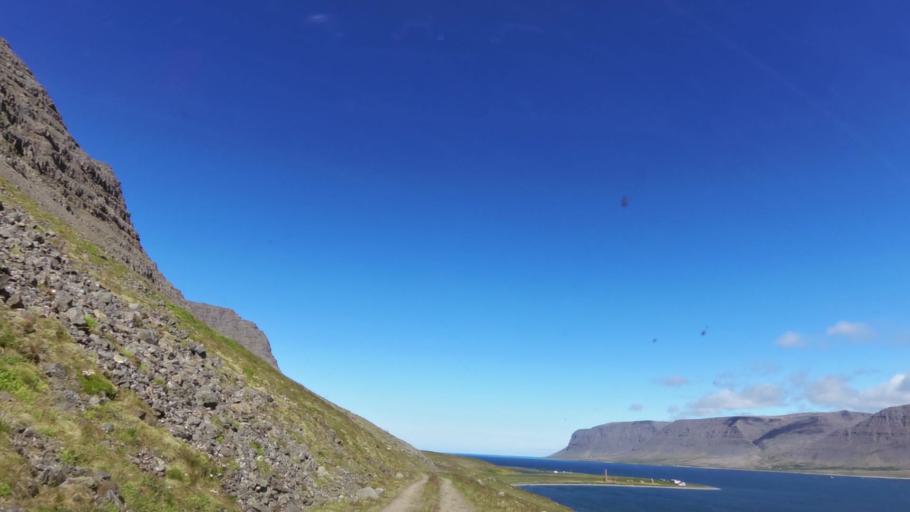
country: IS
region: West
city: Olafsvik
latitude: 65.6335
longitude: -23.9219
